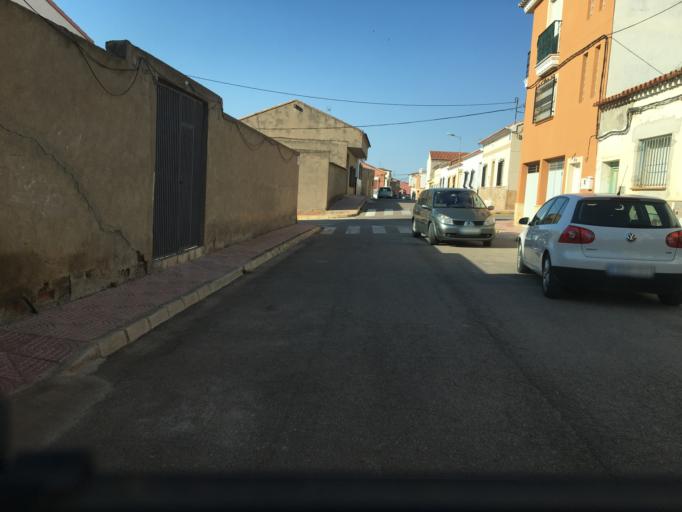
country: ES
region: Murcia
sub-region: Murcia
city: Puerto Lumbreras
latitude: 37.5555
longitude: -1.8147
